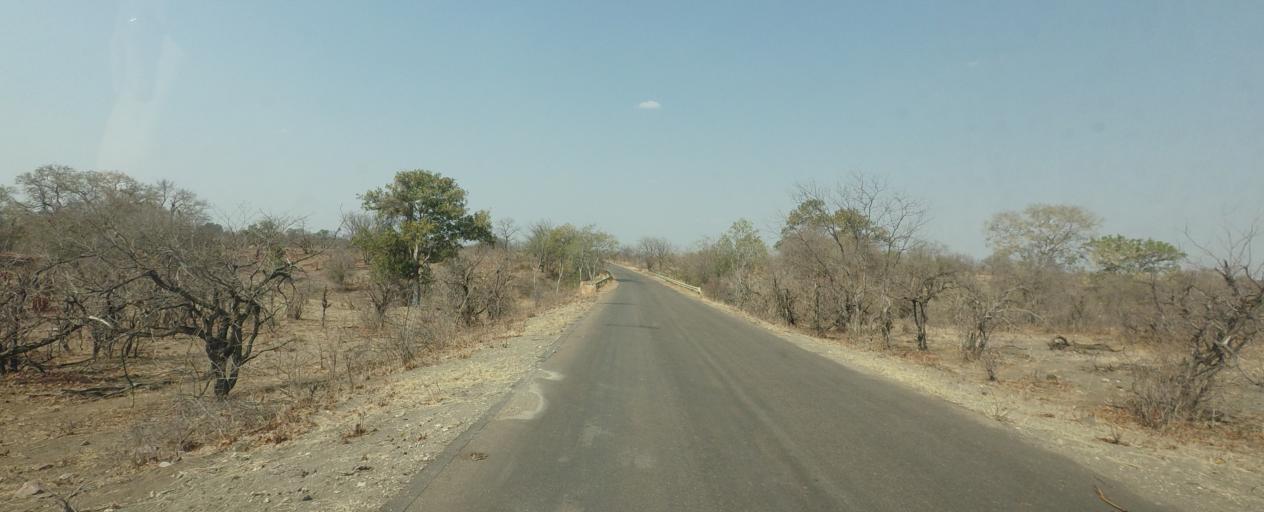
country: ZA
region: Limpopo
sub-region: Mopani District Municipality
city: Giyani
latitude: -23.1784
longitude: 31.3249
